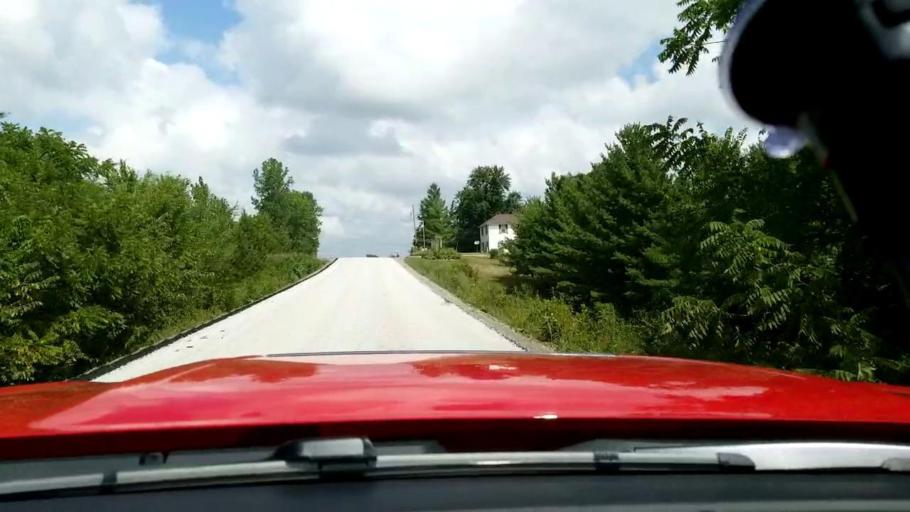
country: US
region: Iowa
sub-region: Decatur County
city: Lamoni
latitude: 40.6449
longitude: -94.0530
